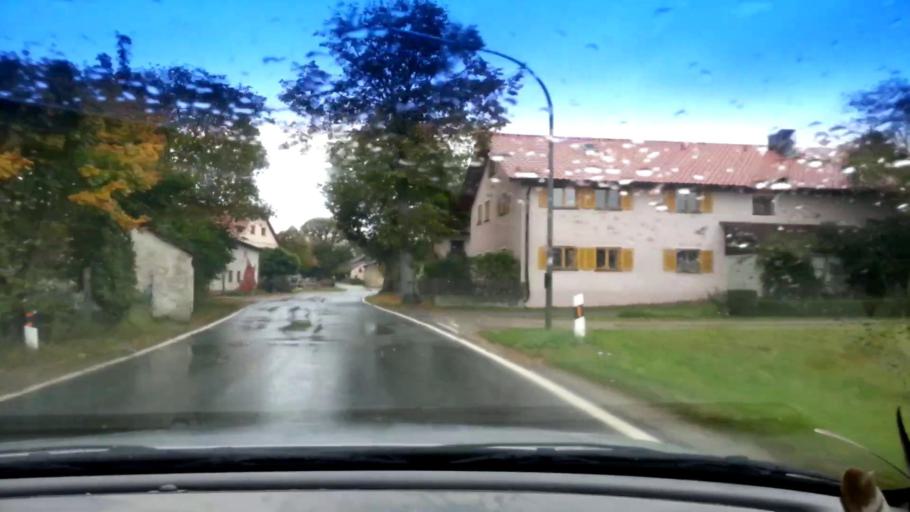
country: DE
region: Bavaria
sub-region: Upper Franconia
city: Poxdorf
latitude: 49.9356
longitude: 11.0804
